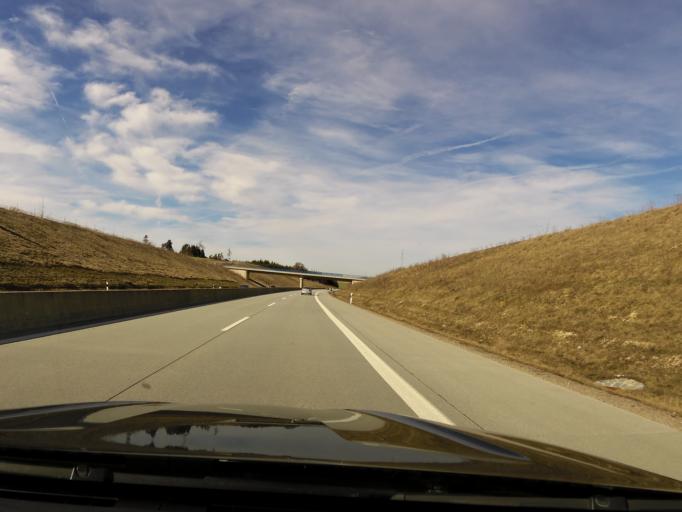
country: DE
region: Bavaria
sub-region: Lower Bavaria
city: Ergoldsbach
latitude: 48.7427
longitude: 12.1438
